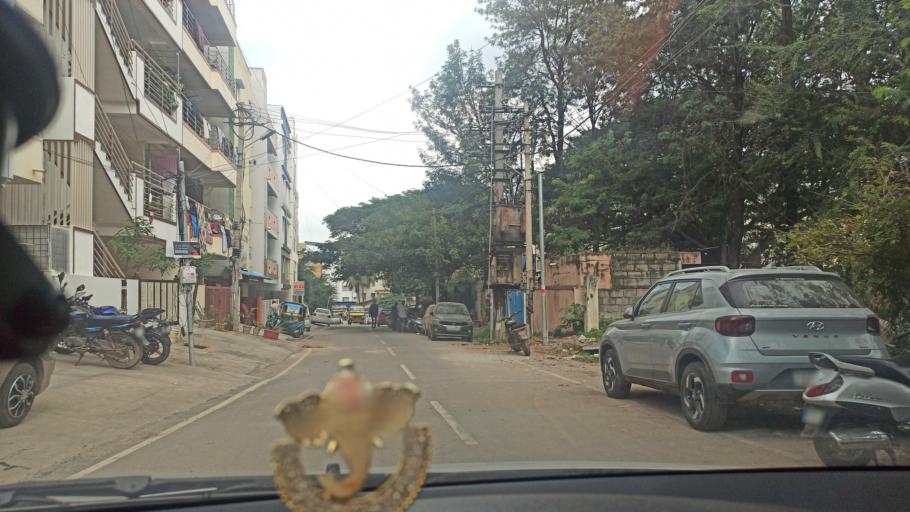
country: IN
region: Karnataka
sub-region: Bangalore Urban
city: Bangalore
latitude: 12.9212
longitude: 77.6473
